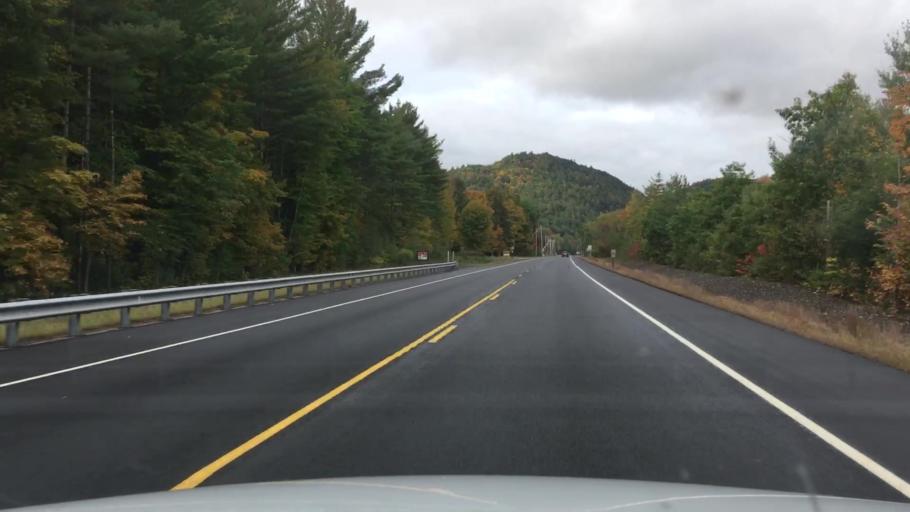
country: US
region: Maine
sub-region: Oxford County
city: Bethel
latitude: 44.3951
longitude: -70.9683
